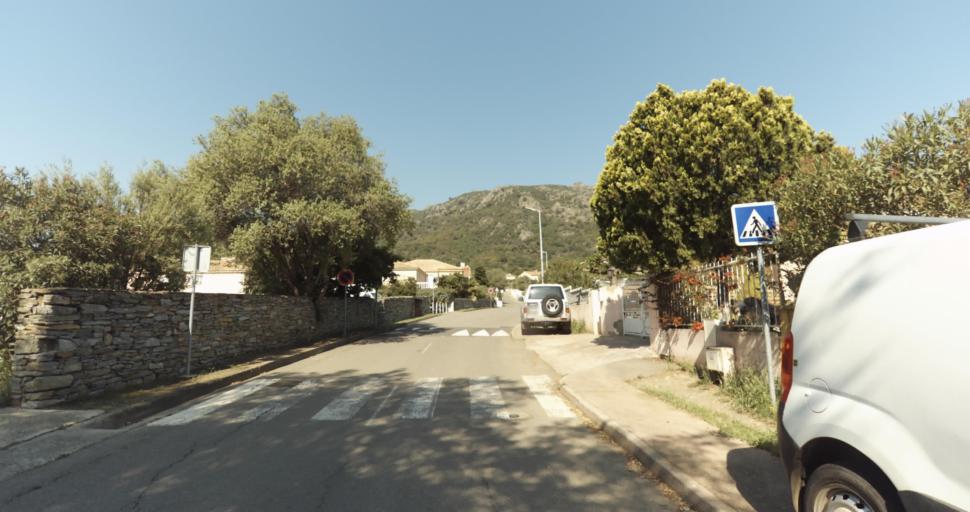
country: FR
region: Corsica
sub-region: Departement de la Haute-Corse
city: Biguglia
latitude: 42.6219
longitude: 9.4275
